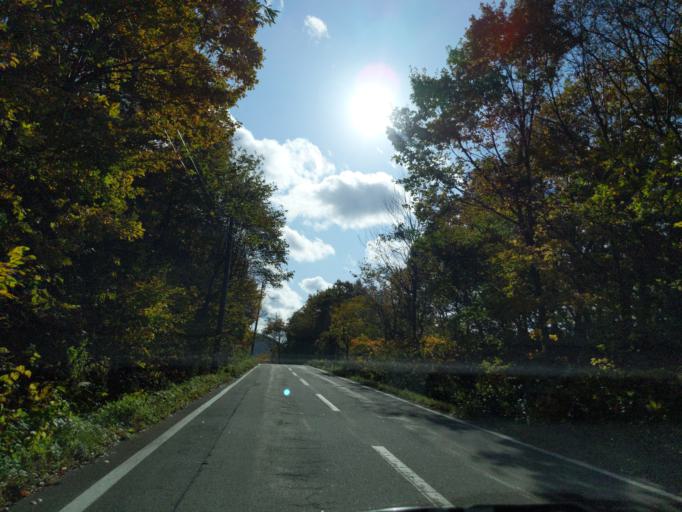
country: JP
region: Iwate
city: Ichinoseki
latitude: 39.0087
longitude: 140.8923
